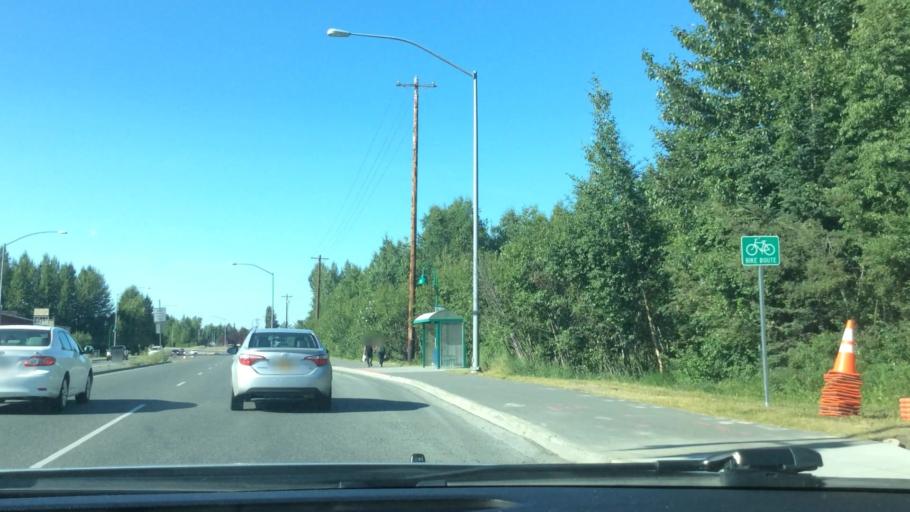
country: US
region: Alaska
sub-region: Anchorage Municipality
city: Anchorage
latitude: 61.1593
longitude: -149.8341
